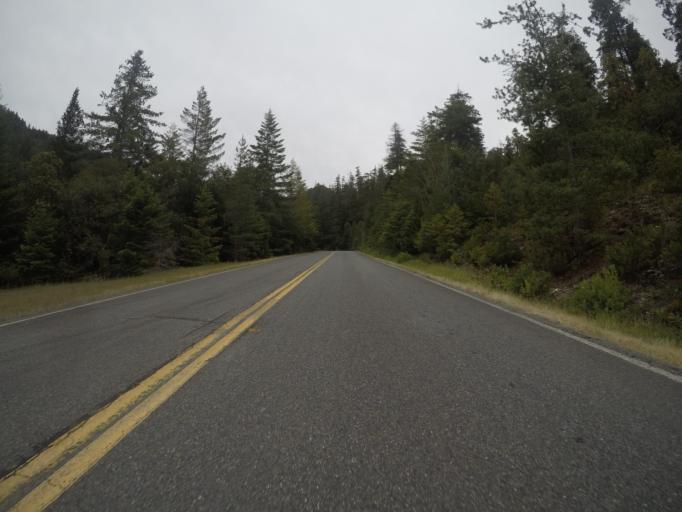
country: US
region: California
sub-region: Del Norte County
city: Bertsch-Oceanview
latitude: 41.7034
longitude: -123.9376
